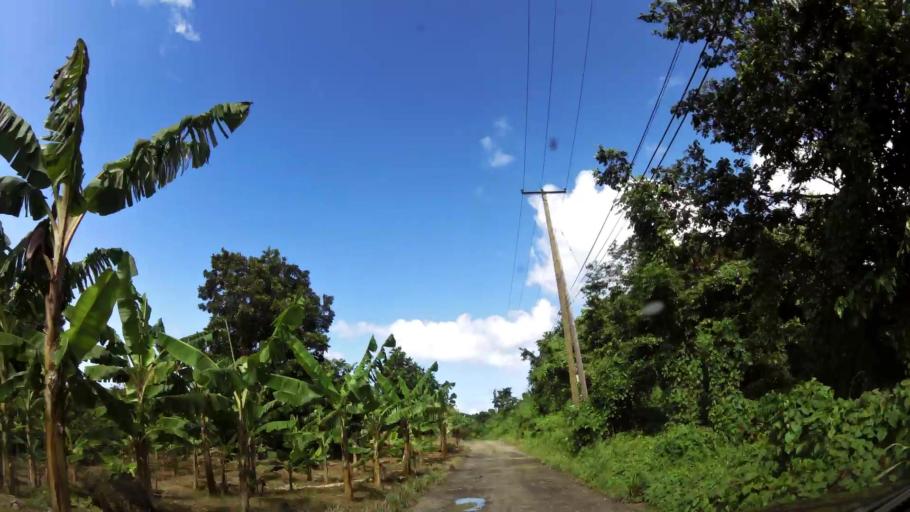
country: DM
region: Saint John
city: Portsmouth
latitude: 15.5591
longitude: -61.4504
